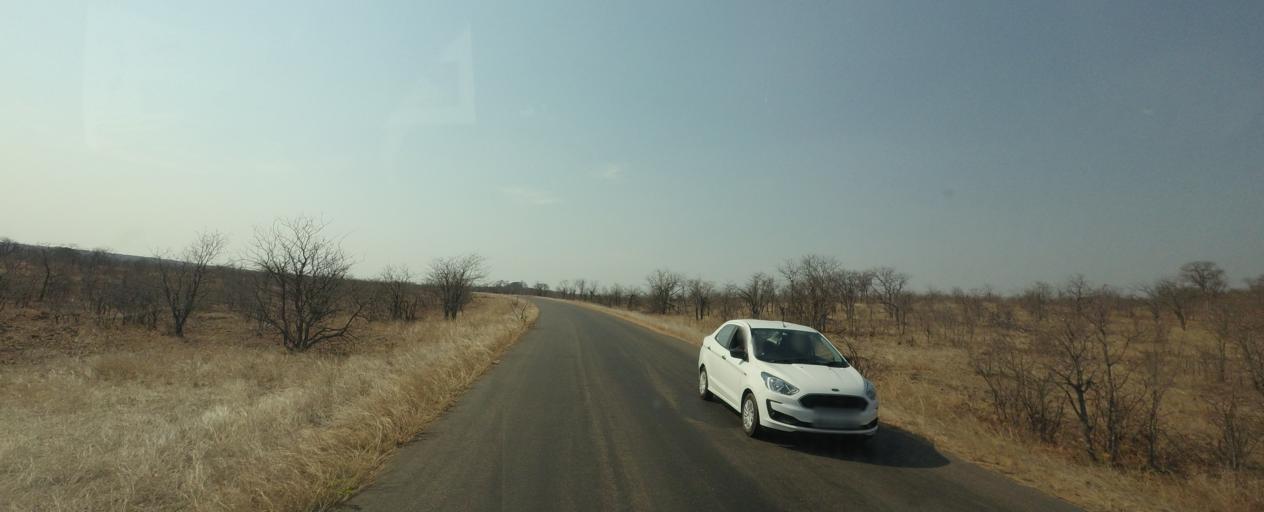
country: ZA
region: Limpopo
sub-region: Mopani District Municipality
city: Phalaborwa
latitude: -23.9677
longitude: 31.6283
